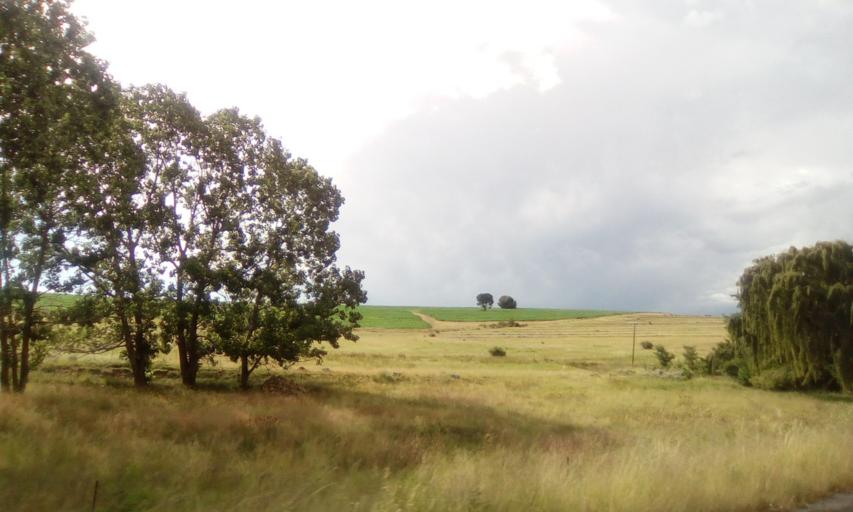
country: ZA
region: Orange Free State
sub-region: Thabo Mofutsanyana District Municipality
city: Ladybrand
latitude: -29.2388
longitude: 27.4493
